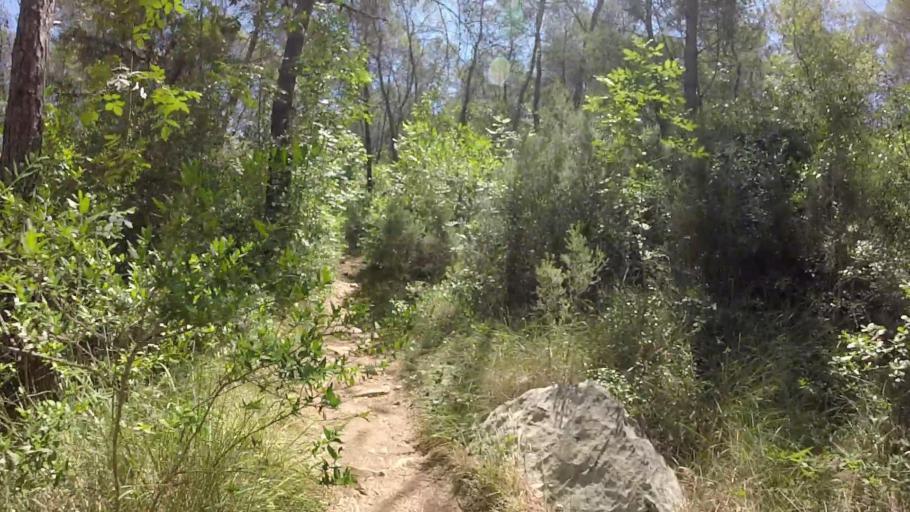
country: FR
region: Provence-Alpes-Cote d'Azur
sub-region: Departement des Alpes-Maritimes
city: Vallauris
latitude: 43.6097
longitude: 7.0481
